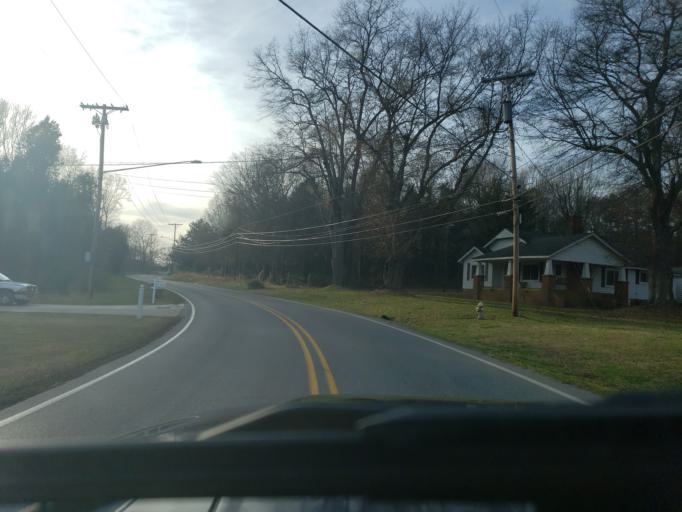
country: US
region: North Carolina
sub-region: Cleveland County
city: Shelby
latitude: 35.2808
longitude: -81.5137
